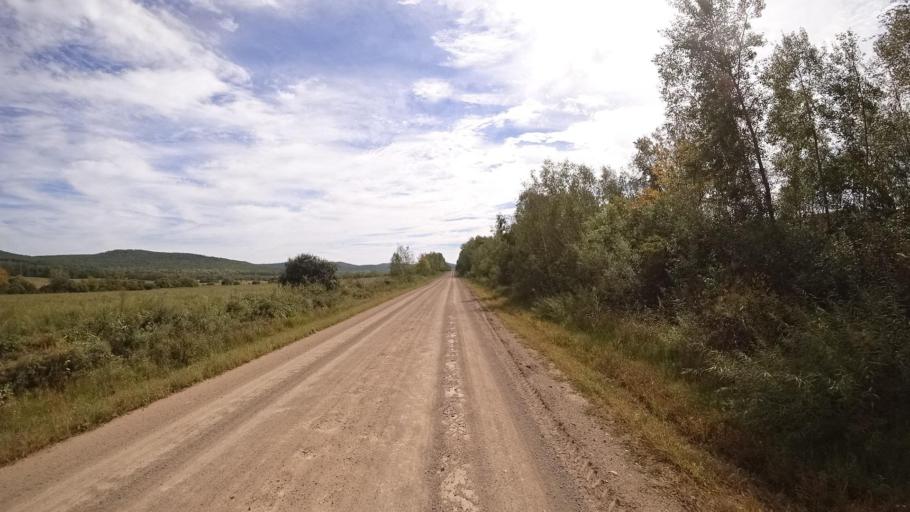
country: RU
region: Primorskiy
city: Yakovlevka
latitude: 44.6129
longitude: 133.5991
